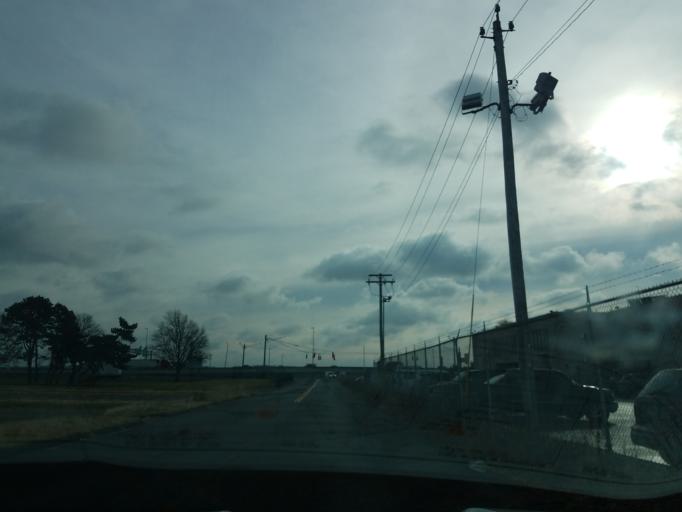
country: US
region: Connecticut
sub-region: New Haven County
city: New Haven
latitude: 41.2899
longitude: -72.9256
